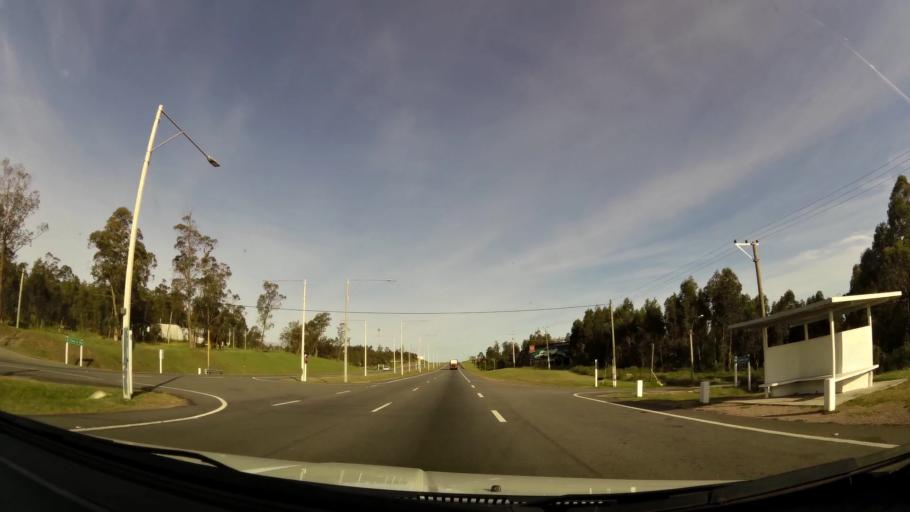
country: UY
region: Canelones
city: La Floresta
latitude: -34.7797
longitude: -55.5534
